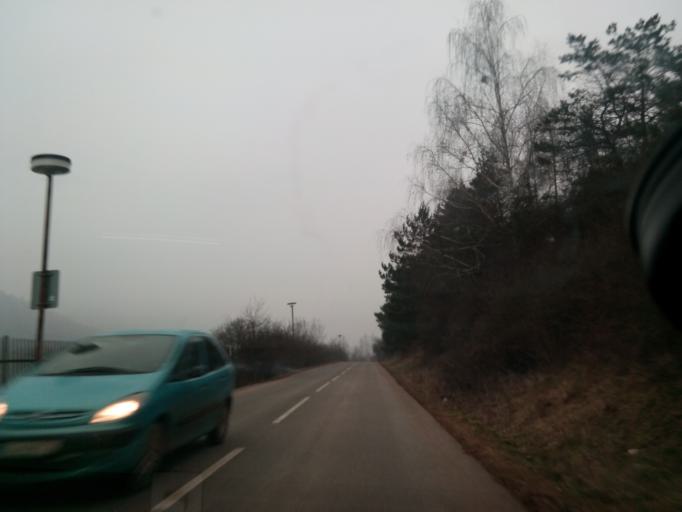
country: SK
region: Kosicky
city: Kosice
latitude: 48.7042
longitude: 21.1570
